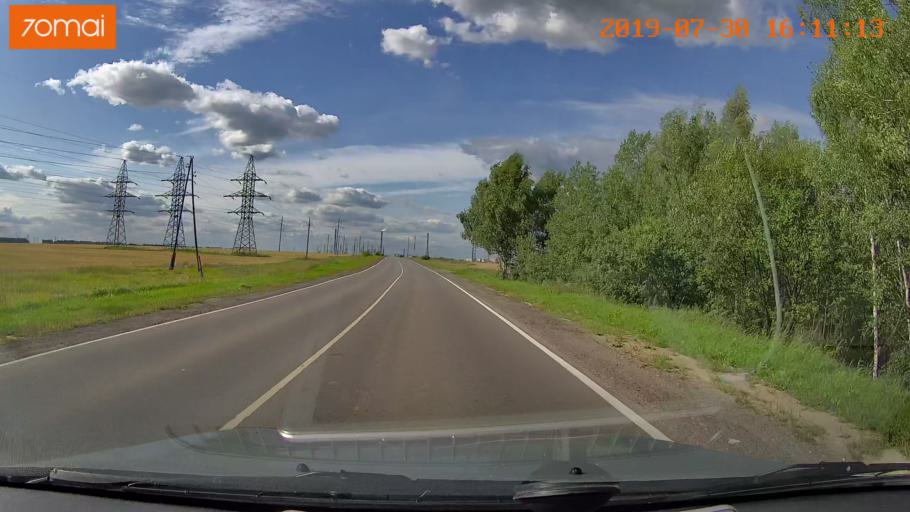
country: RU
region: Moskovskaya
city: Lopatinskiy
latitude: 55.2726
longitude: 38.7132
